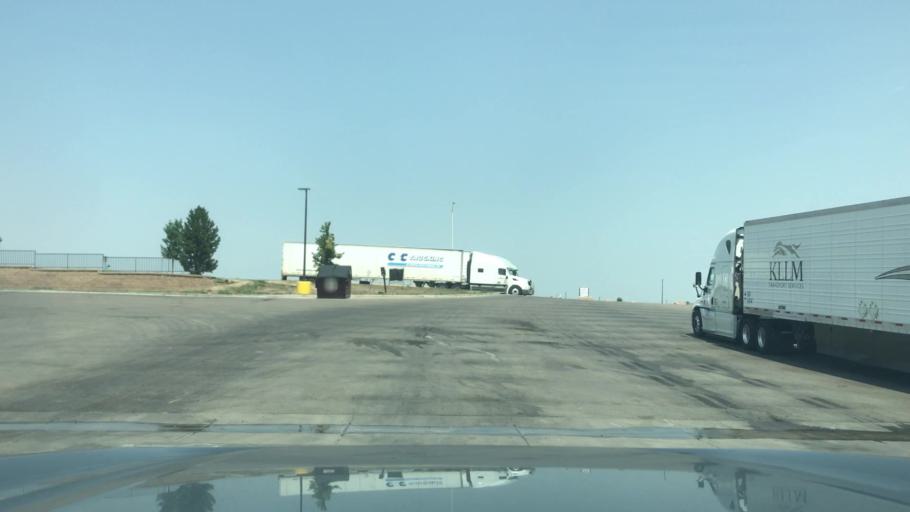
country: US
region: Colorado
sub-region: Pueblo County
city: Pueblo
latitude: 38.3424
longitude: -104.6236
